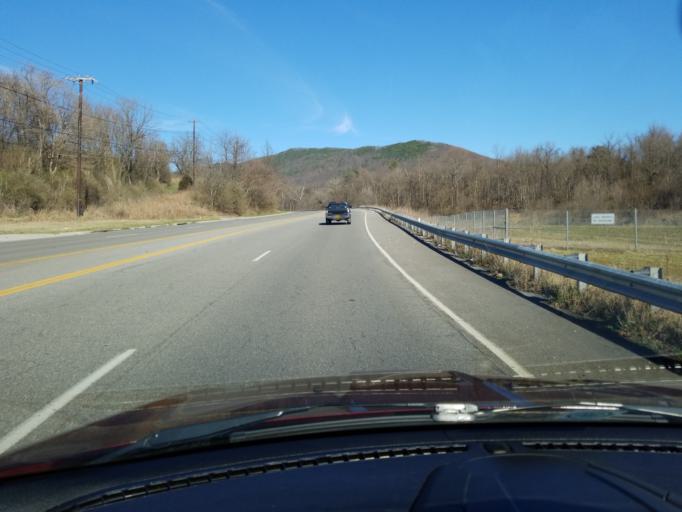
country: US
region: Virginia
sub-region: Roanoke County
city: Hollins
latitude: 37.3233
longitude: -79.9313
